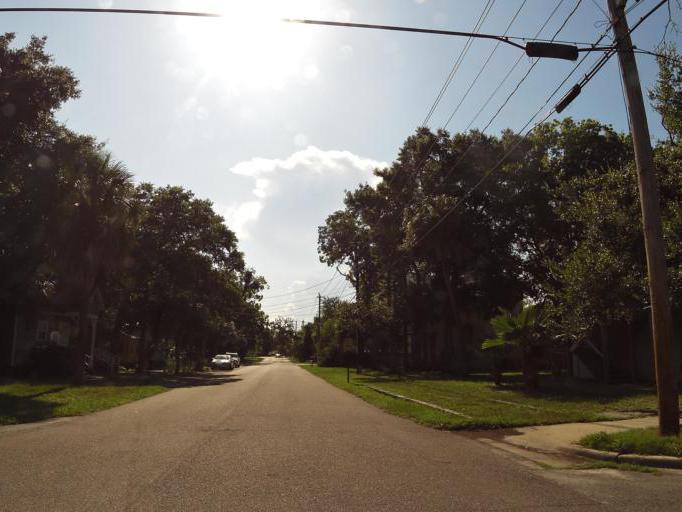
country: US
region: Florida
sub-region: Nassau County
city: Fernandina Beach
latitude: 30.6685
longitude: -81.4617
